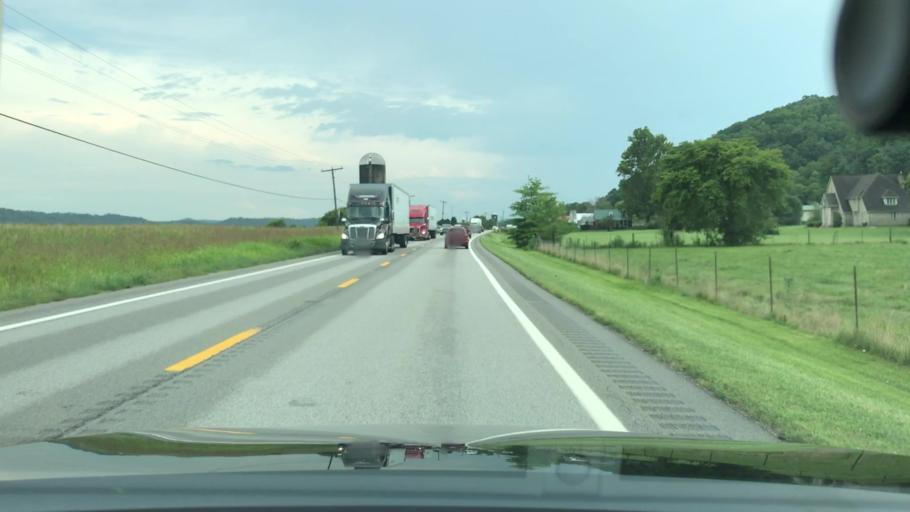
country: US
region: West Virginia
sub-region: Putnam County
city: Buffalo
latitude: 38.7368
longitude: -81.9755
